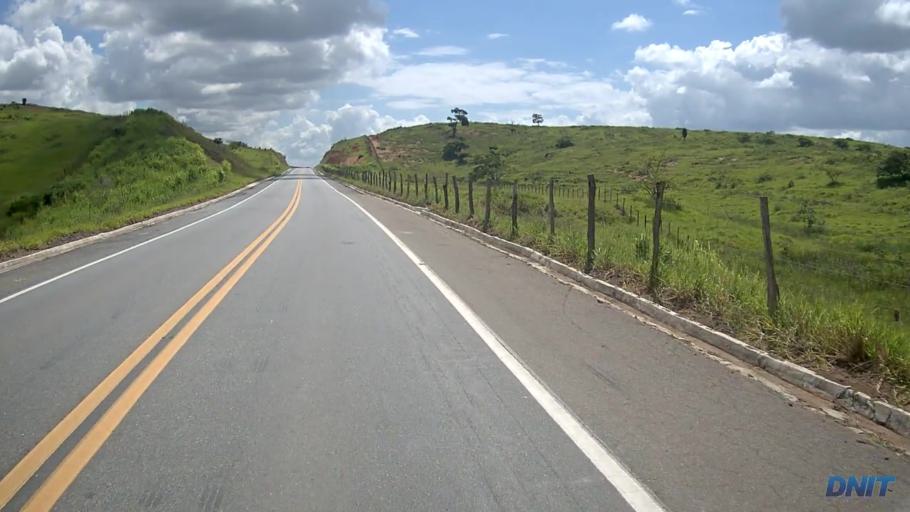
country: BR
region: Minas Gerais
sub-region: Governador Valadares
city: Governador Valadares
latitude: -18.9928
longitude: -42.1165
